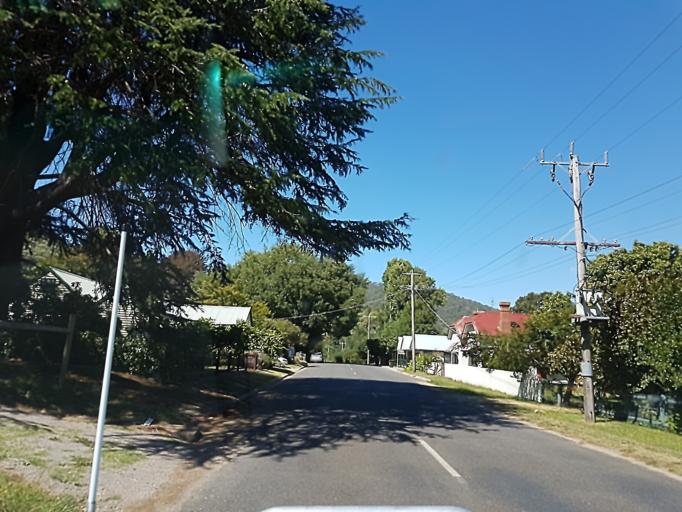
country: AU
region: Victoria
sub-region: Alpine
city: Mount Beauty
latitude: -36.7724
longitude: 146.9819
